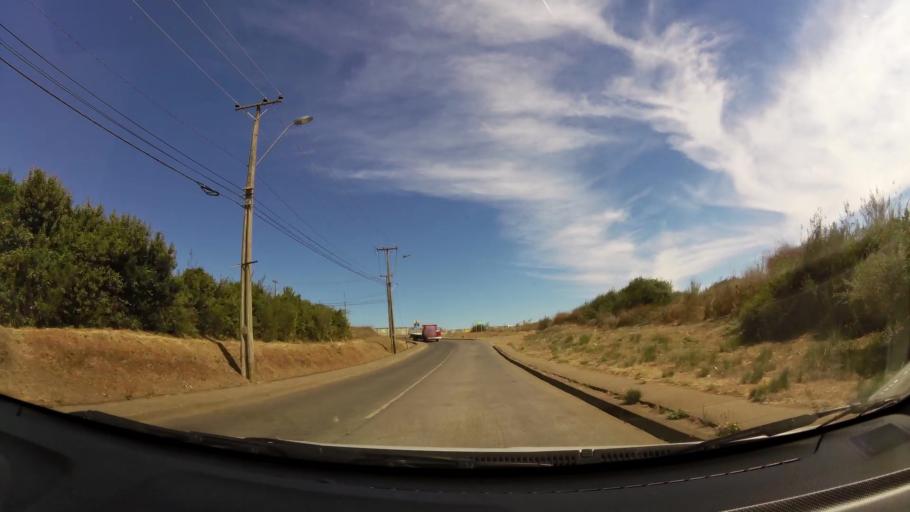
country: CL
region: Biobio
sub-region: Provincia de Concepcion
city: Talcahuano
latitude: -36.7090
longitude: -73.1283
